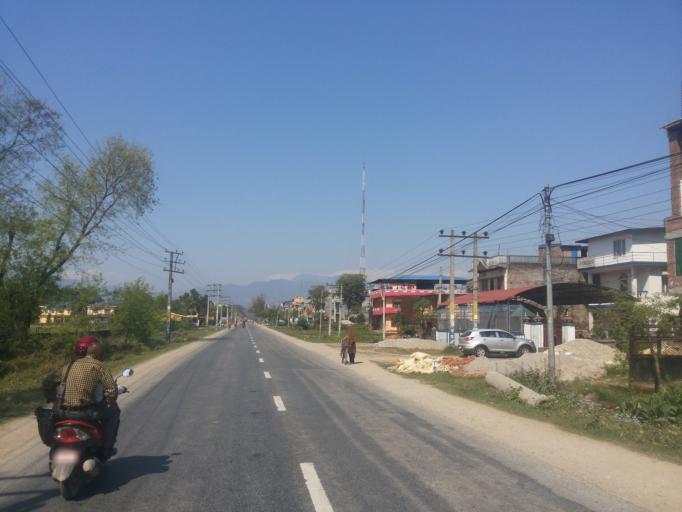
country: NP
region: Central Region
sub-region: Narayani Zone
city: Bharatpur
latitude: 27.6828
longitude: 84.4395
